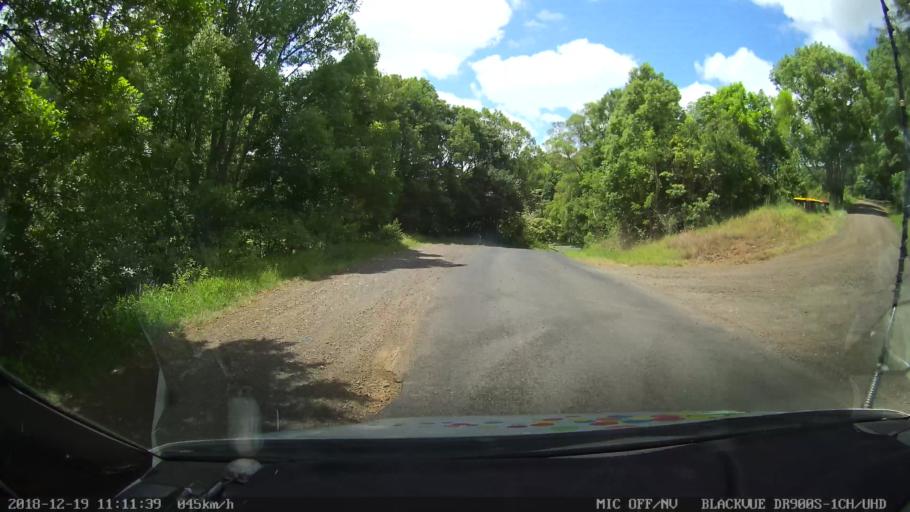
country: AU
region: New South Wales
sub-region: Lismore Municipality
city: Nimbin
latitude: -28.6445
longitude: 153.2586
